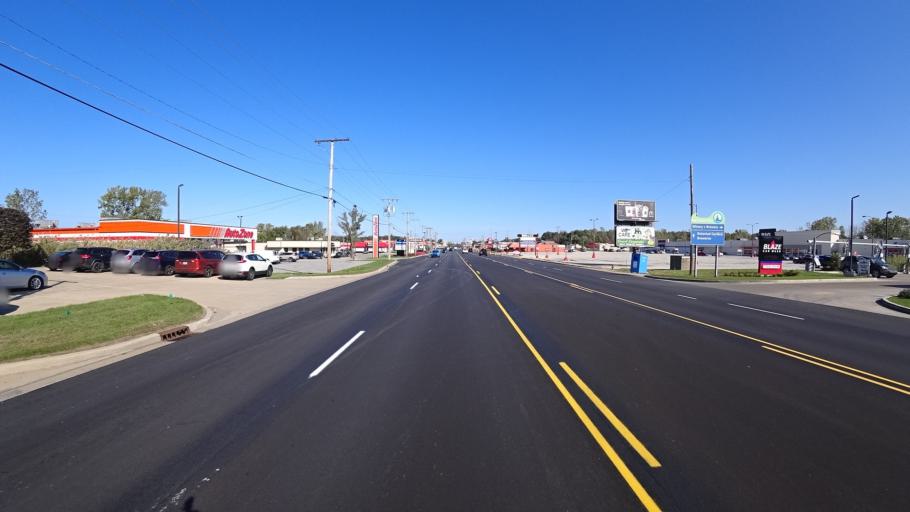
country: US
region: Indiana
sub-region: LaPorte County
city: Michigan City
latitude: 41.6775
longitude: -86.8940
